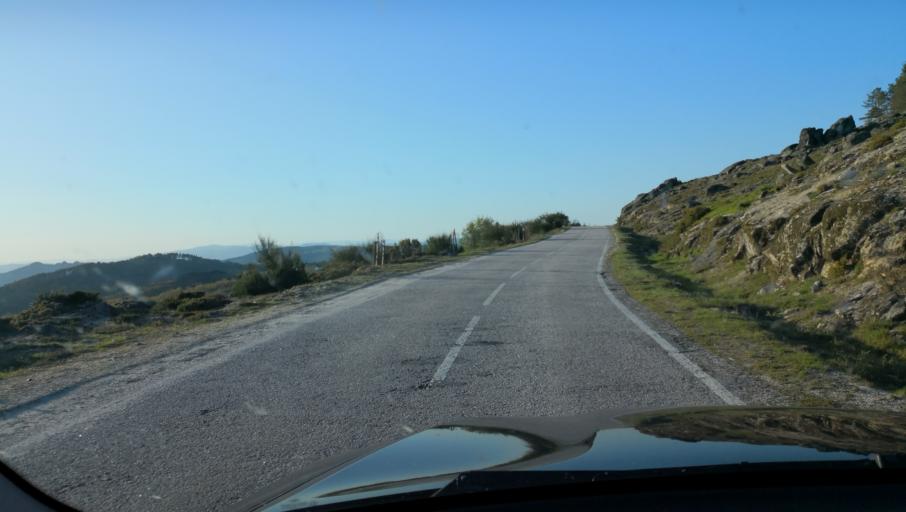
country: PT
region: Vila Real
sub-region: Vila Real
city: Vila Real
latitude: 41.3892
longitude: -7.8272
